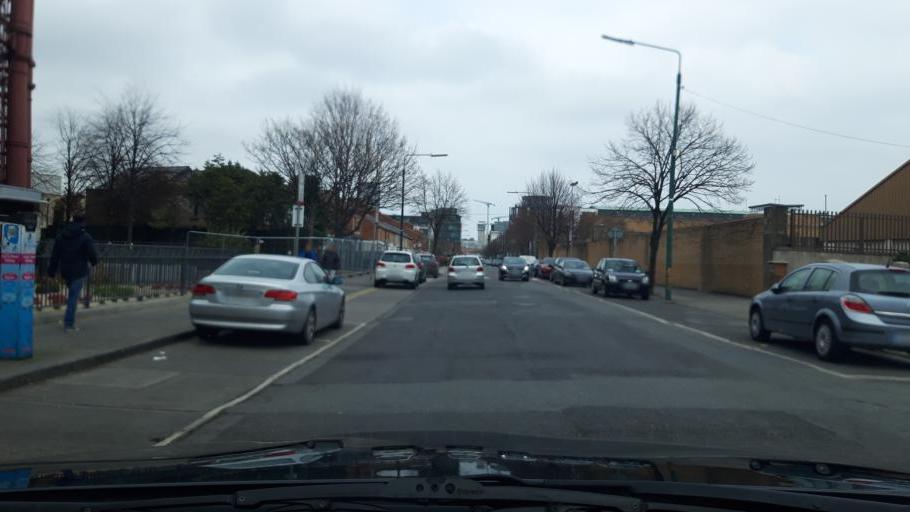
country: IE
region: Leinster
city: Ringsend
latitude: 53.3385
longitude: -6.2332
